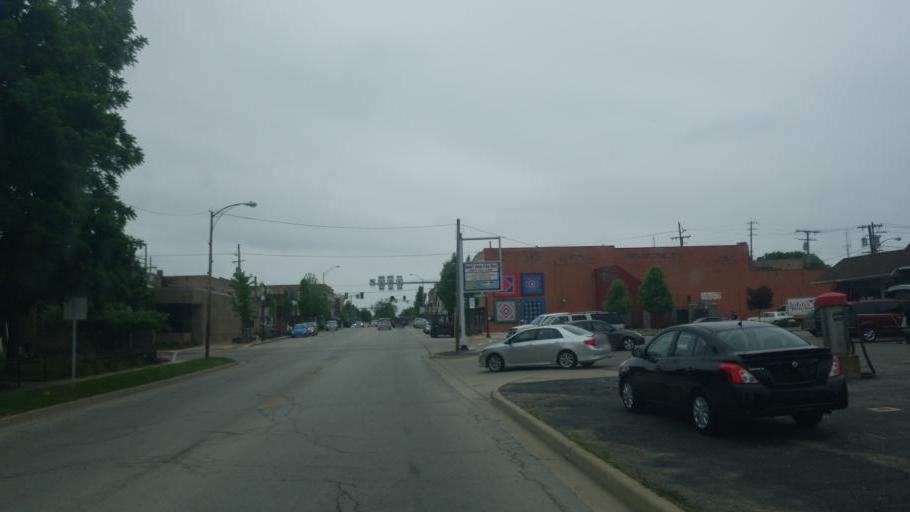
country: US
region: Indiana
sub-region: Elkhart County
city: Nappanee
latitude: 41.4441
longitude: -86.0013
